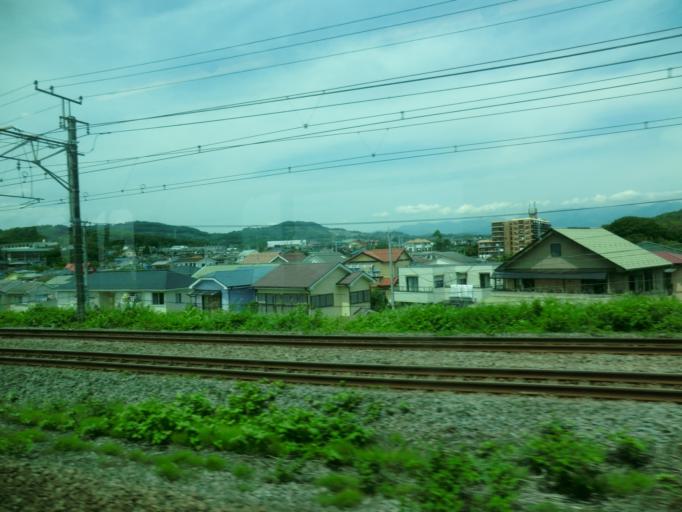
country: JP
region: Kanagawa
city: Ninomiya
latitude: 35.2920
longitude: 139.2368
